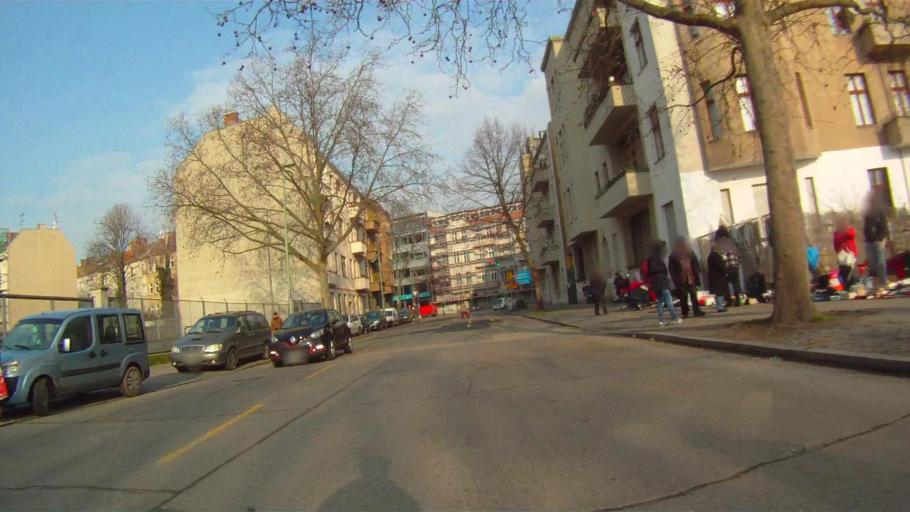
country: DE
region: Berlin
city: Treptow Bezirk
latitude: 52.4673
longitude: 13.4455
